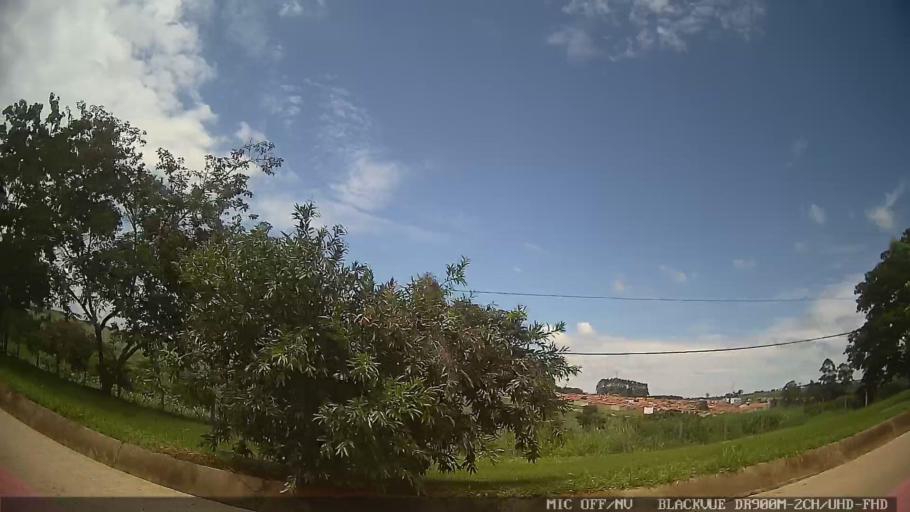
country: BR
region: Sao Paulo
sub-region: Laranjal Paulista
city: Laranjal Paulista
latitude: -23.0671
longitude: -47.8253
